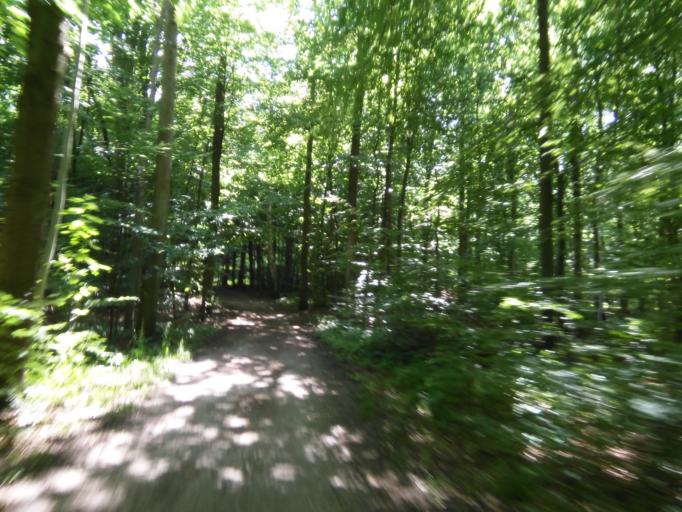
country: DK
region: Central Jutland
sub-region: Arhus Kommune
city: Arhus
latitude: 56.1338
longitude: 10.2052
